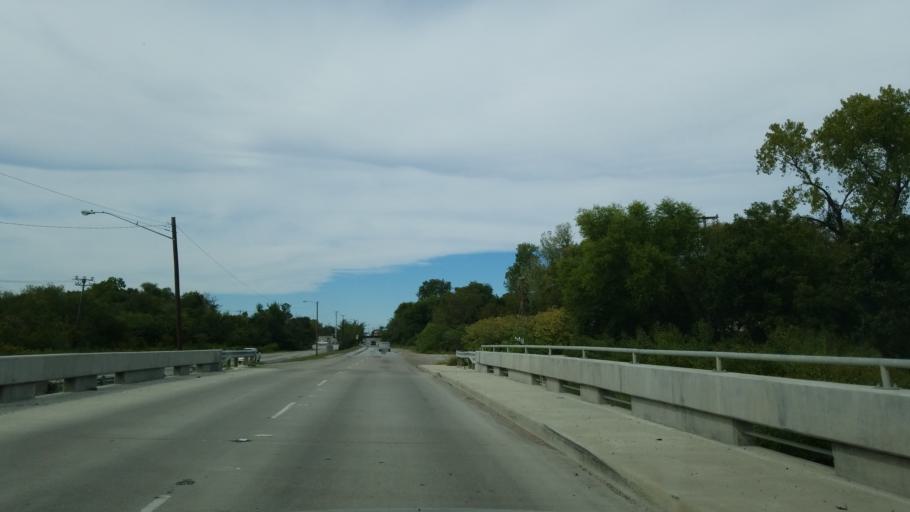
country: US
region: Texas
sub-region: Dallas County
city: Dallas
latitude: 32.7554
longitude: -96.7378
